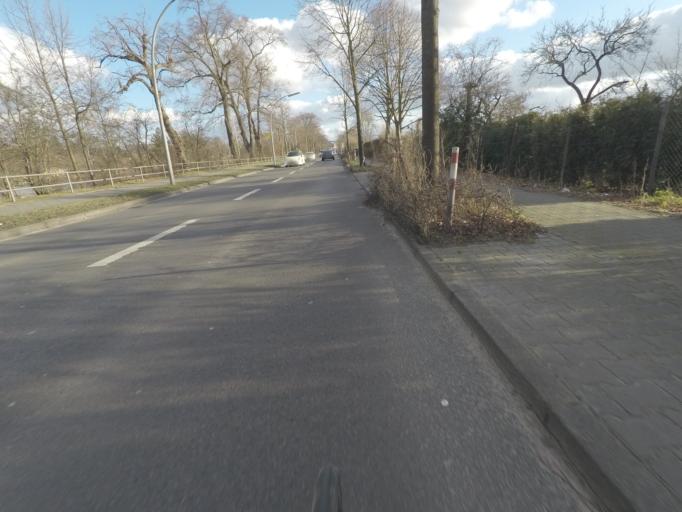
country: DE
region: Berlin
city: Reinickendorf
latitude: 52.5450
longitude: 13.3205
